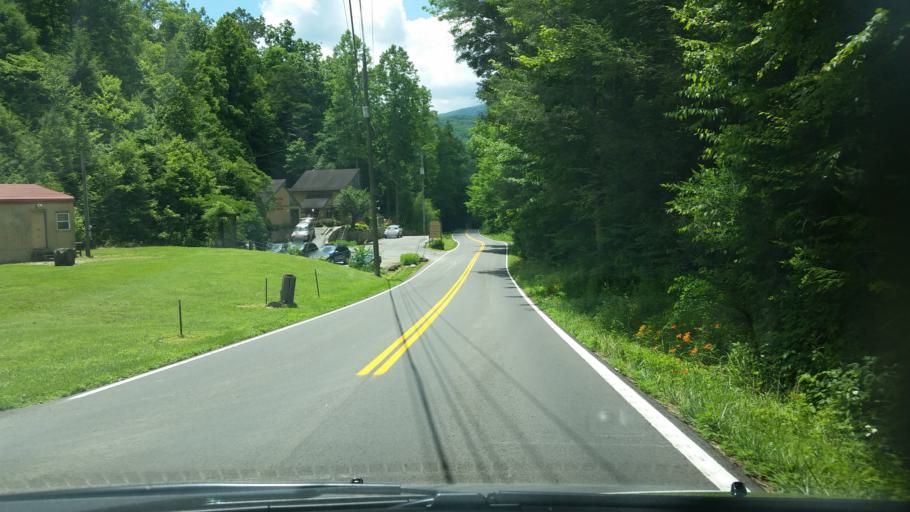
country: US
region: Tennessee
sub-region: Sevier County
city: Gatlinburg
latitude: 35.7411
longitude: -83.4286
